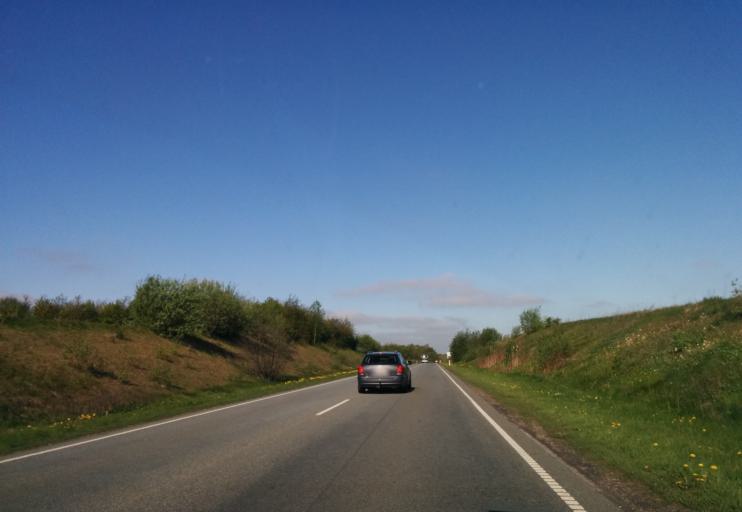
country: DK
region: Central Jutland
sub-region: Arhus Kommune
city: Kolt
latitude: 56.1186
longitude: 10.0934
